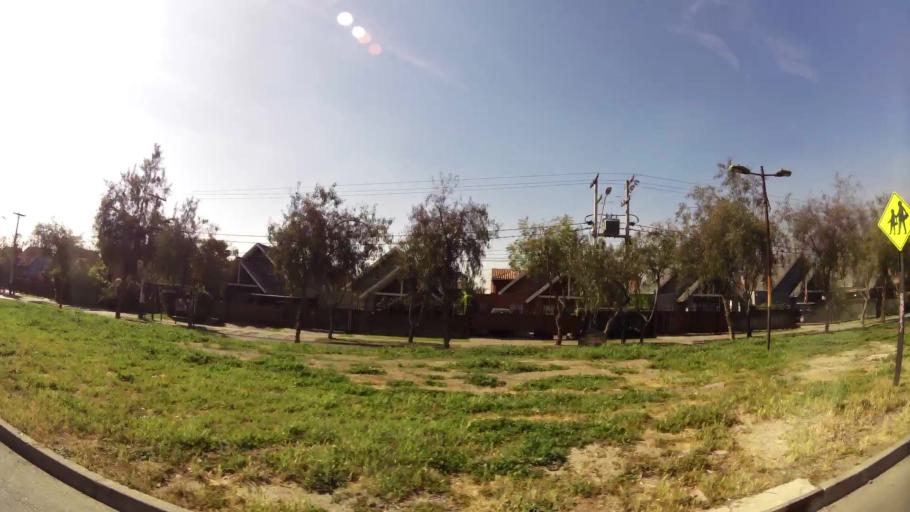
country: CL
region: Santiago Metropolitan
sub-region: Provincia de Santiago
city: Villa Presidente Frei, Nunoa, Santiago, Chile
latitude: -33.4858
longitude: -70.5603
